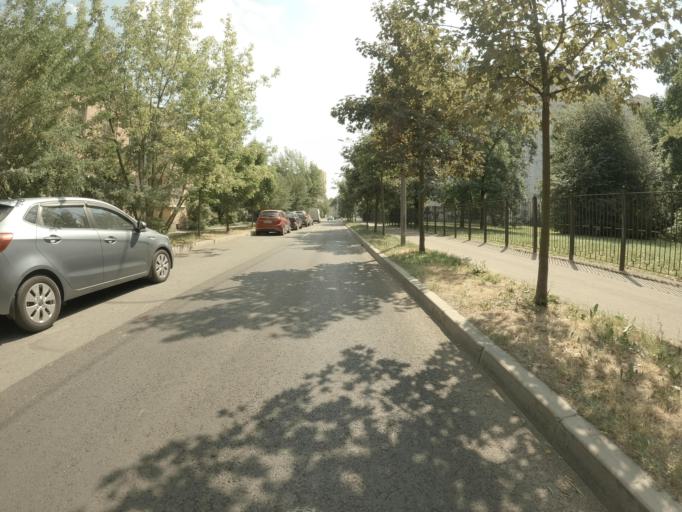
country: RU
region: St.-Petersburg
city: Avtovo
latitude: 59.8941
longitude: 30.2606
